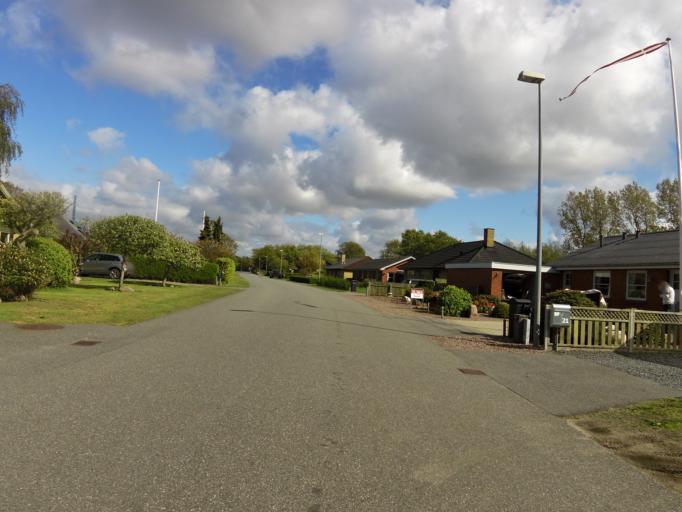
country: DK
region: South Denmark
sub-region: Esbjerg Kommune
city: Ribe
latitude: 55.2752
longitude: 8.7234
